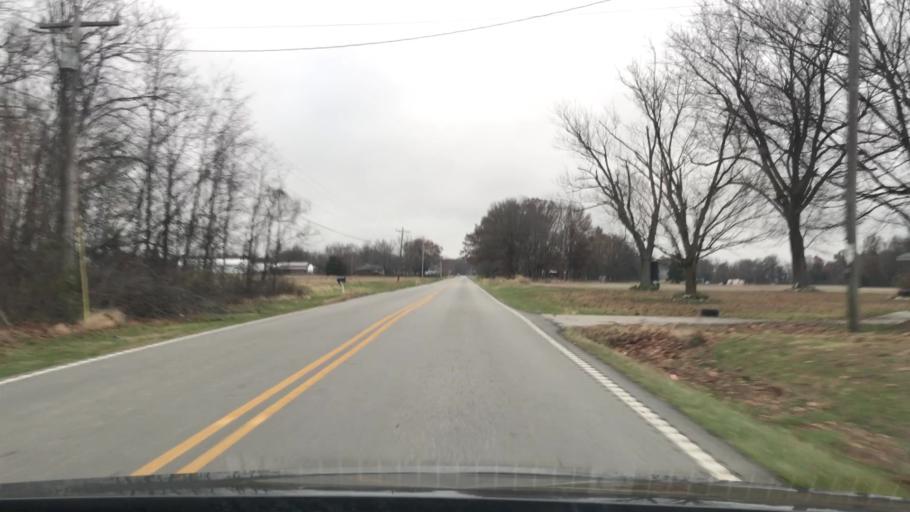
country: US
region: Kentucky
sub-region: Todd County
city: Guthrie
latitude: 36.7162
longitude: -87.1920
